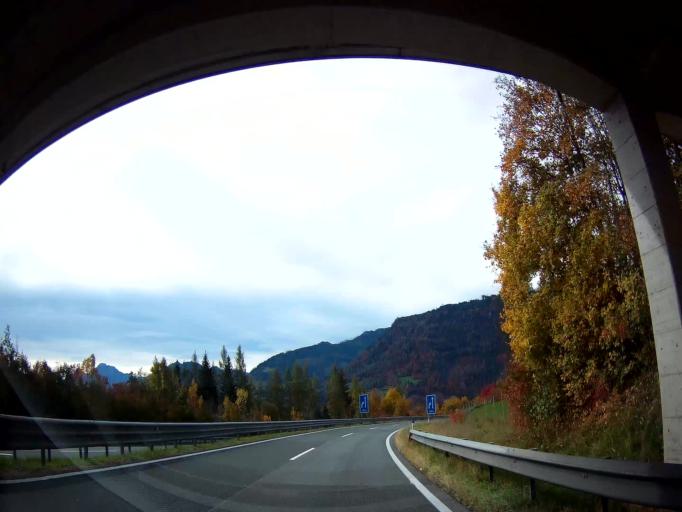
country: AT
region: Salzburg
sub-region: Politischer Bezirk Sankt Johann im Pongau
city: Bischofshofen
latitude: 47.4372
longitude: 13.2337
